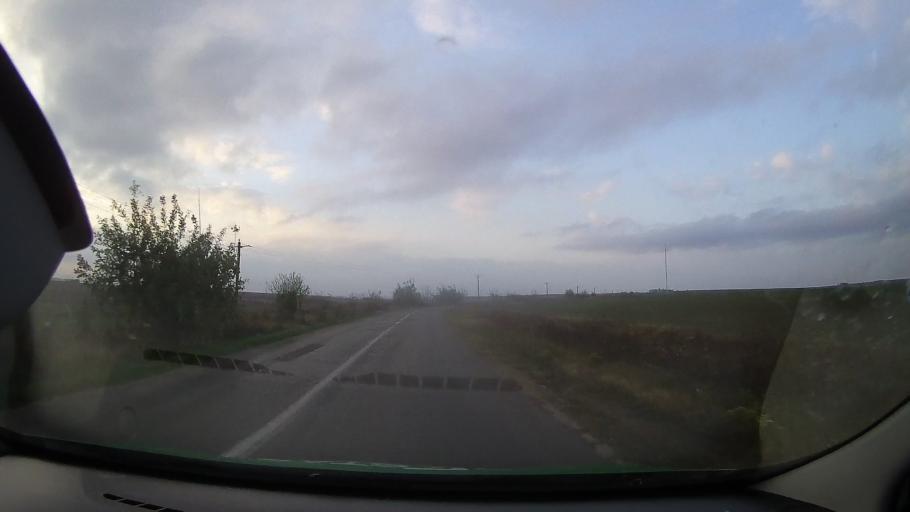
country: RO
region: Constanta
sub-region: Comuna Dobromir
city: Dobromir
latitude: 44.0355
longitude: 27.7603
